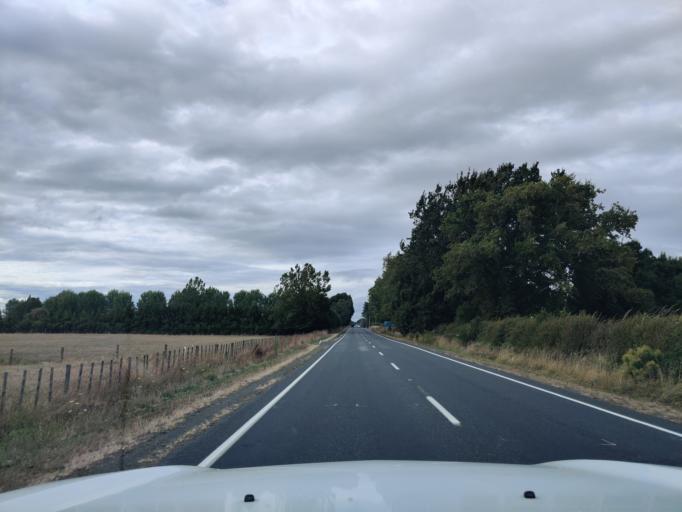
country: NZ
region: Waikato
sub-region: Waipa District
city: Cambridge
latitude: -37.8533
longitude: 175.4535
